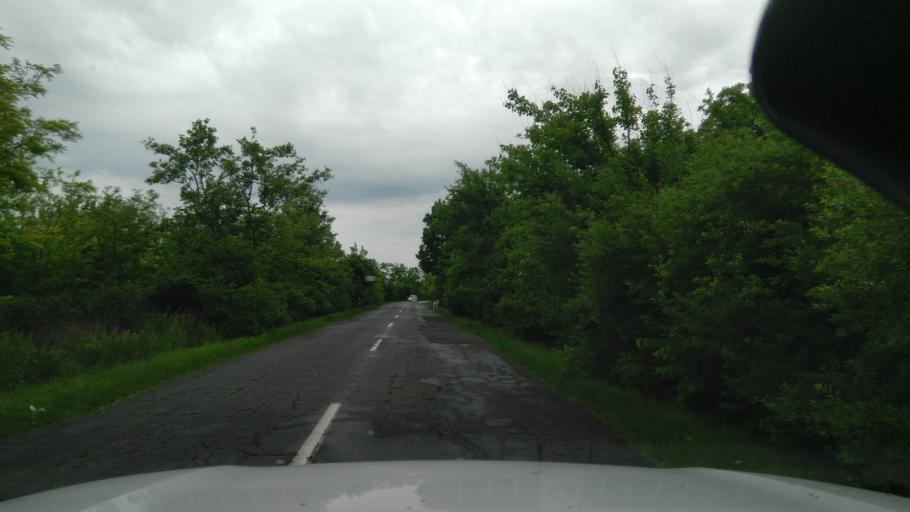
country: HU
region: Bekes
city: Bekescsaba
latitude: 46.6763
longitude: 21.1711
